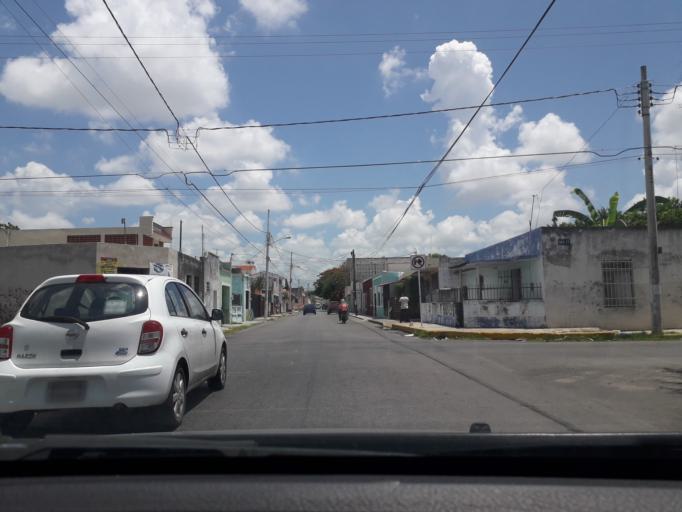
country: MX
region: Yucatan
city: Merida
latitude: 20.9557
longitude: -89.6204
